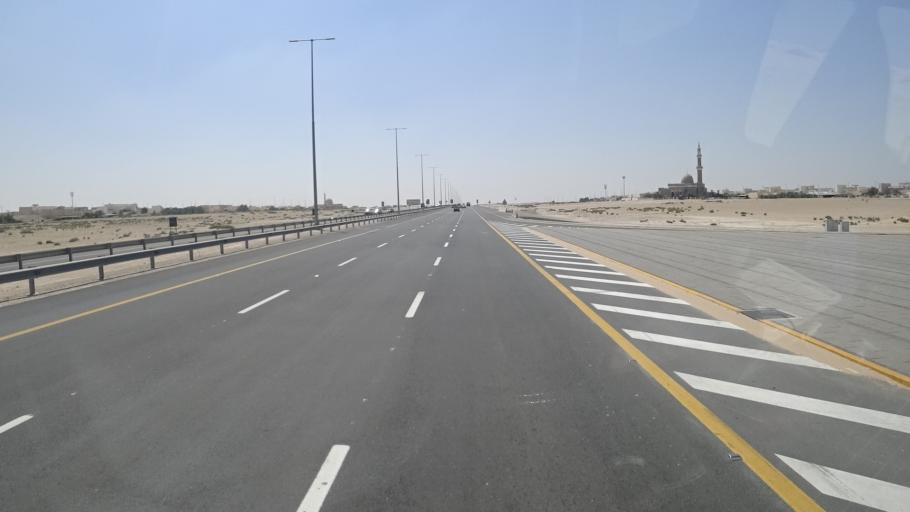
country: AE
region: Abu Dhabi
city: Abu Dhabi
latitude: 24.3338
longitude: 54.6960
